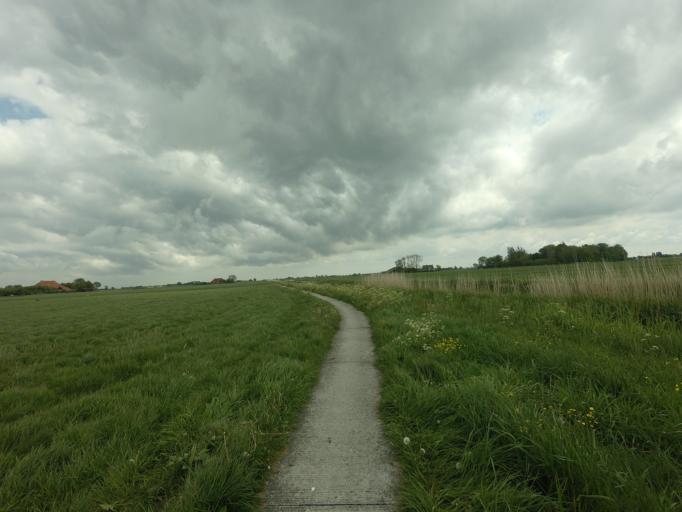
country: NL
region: Friesland
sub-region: Gemeente Littenseradiel
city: Makkum
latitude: 53.0924
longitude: 5.6326
